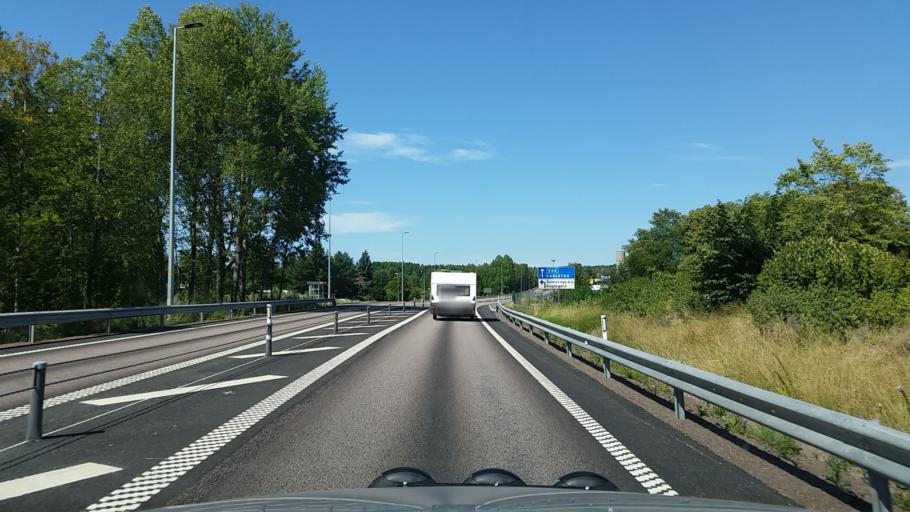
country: SE
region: Vaestra Goetaland
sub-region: Melleruds Kommun
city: Mellerud
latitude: 58.8761
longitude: 12.5675
